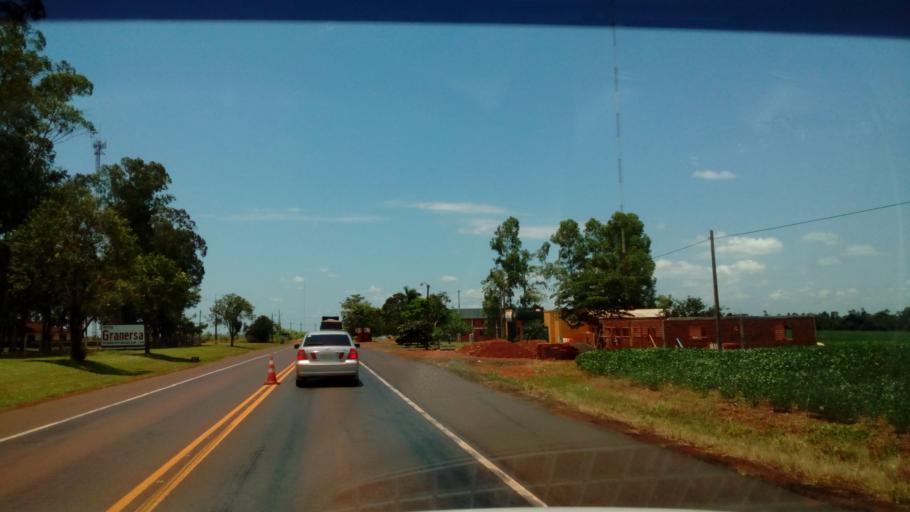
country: PY
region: Alto Parana
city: Santa Rita
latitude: -25.8665
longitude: -55.1175
